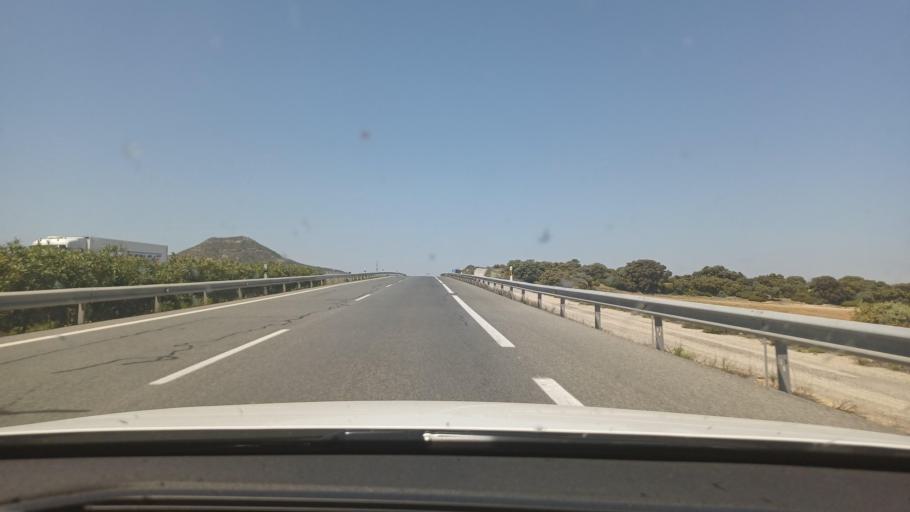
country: ES
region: Castille-La Mancha
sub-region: Provincia de Albacete
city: Corral-Rubio
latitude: 38.8979
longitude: -1.4436
